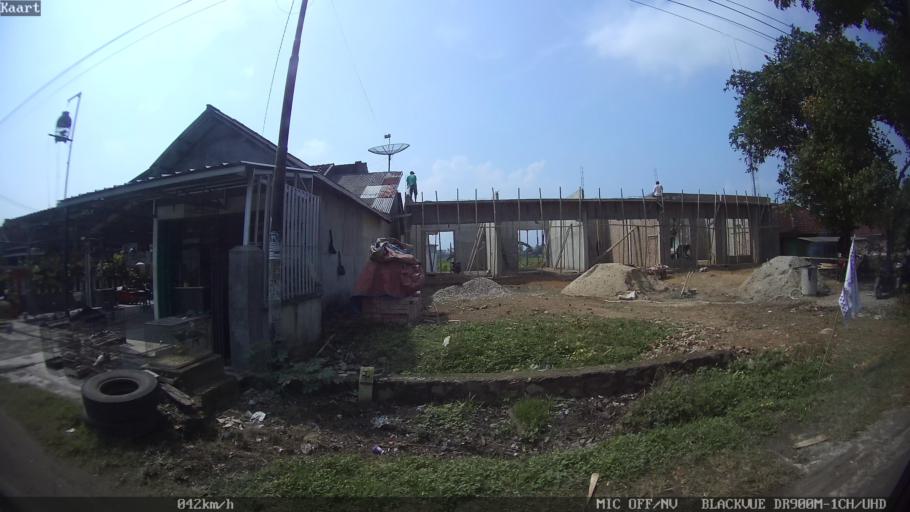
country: ID
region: Lampung
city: Gadingrejo
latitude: -5.3739
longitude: 105.0432
